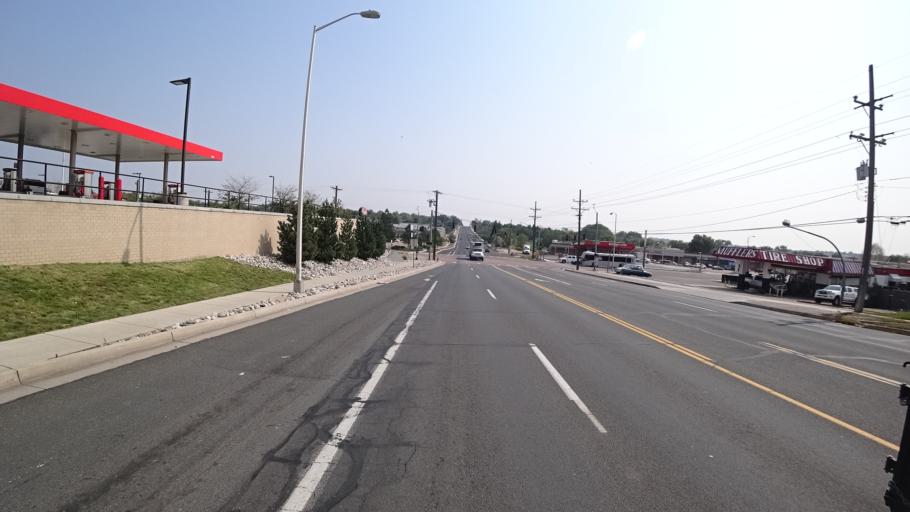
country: US
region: Colorado
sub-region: El Paso County
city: Colorado Springs
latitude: 38.8254
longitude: -104.7813
